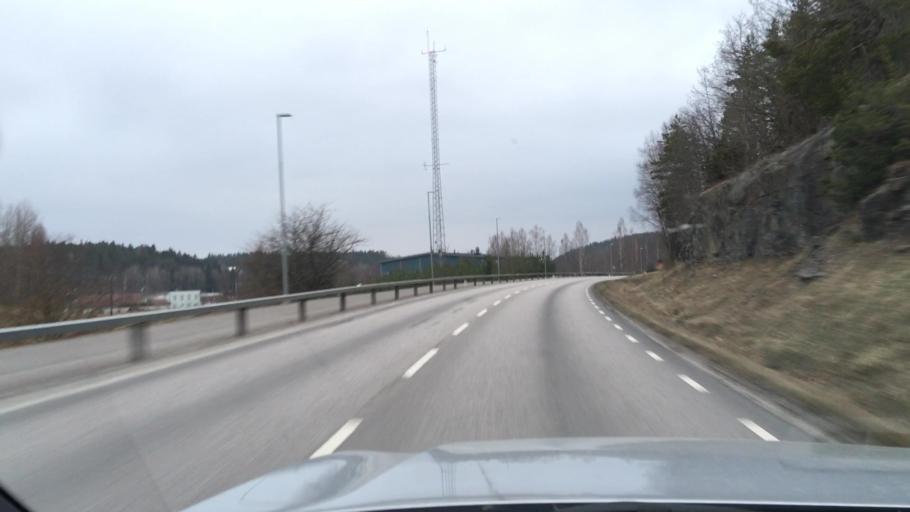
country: SE
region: OEstergoetland
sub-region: Valdemarsviks Kommun
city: Valdemarsvik
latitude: 58.2069
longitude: 16.5844
